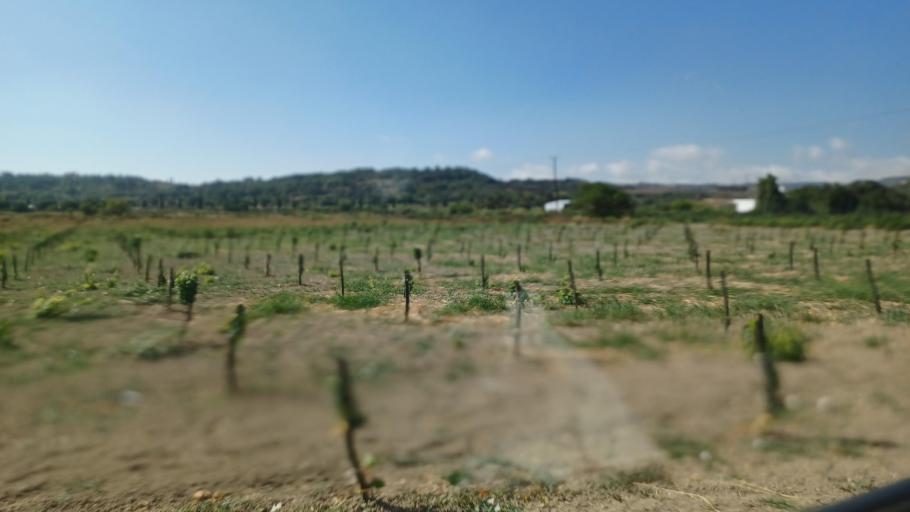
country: CY
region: Pafos
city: Tala
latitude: 34.8858
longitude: 32.4943
